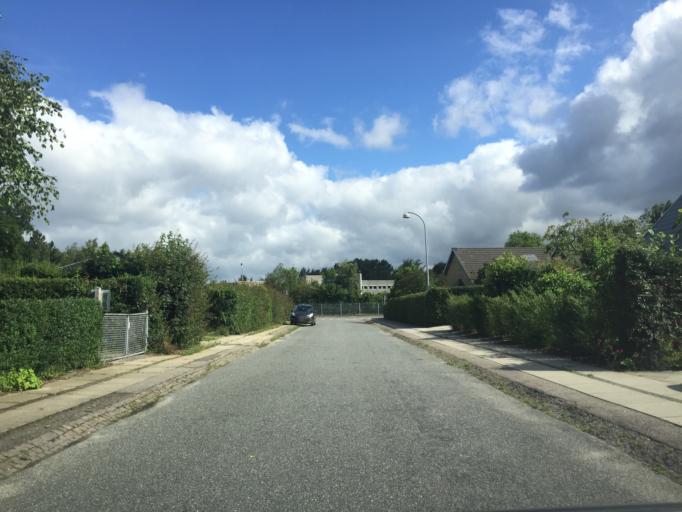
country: DK
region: Capital Region
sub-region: Brondby Kommune
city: Brondbyvester
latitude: 55.6543
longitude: 12.4135
